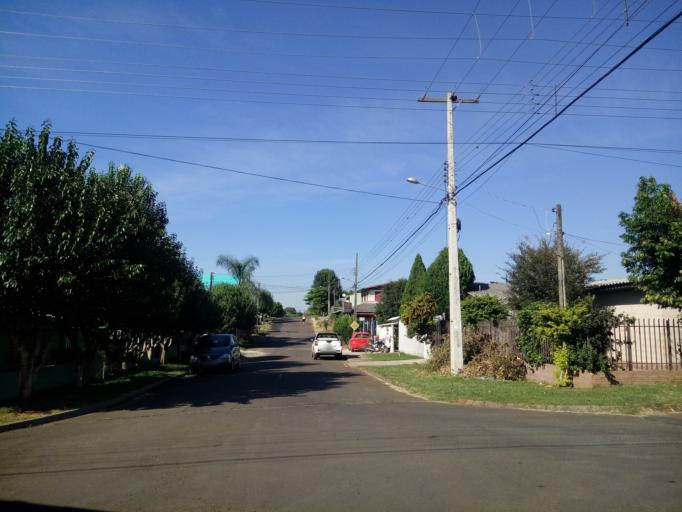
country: BR
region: Santa Catarina
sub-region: Chapeco
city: Chapeco
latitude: -27.0998
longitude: -52.6665
